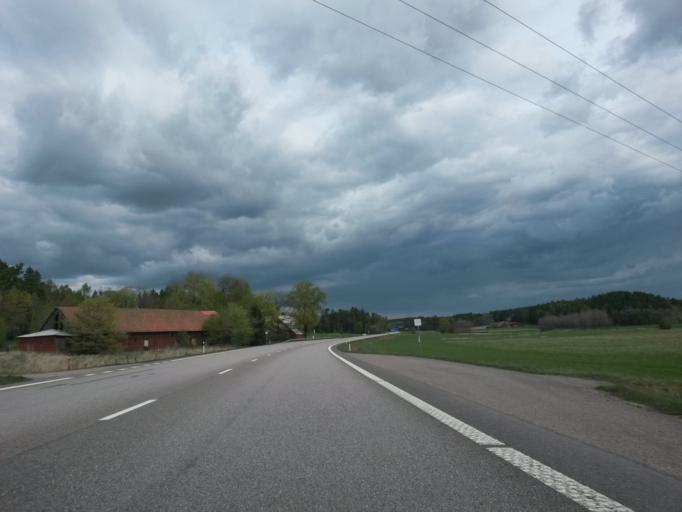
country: SE
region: Vaestra Goetaland
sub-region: Vargarda Kommun
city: Vargarda
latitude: 58.0855
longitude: 12.8213
